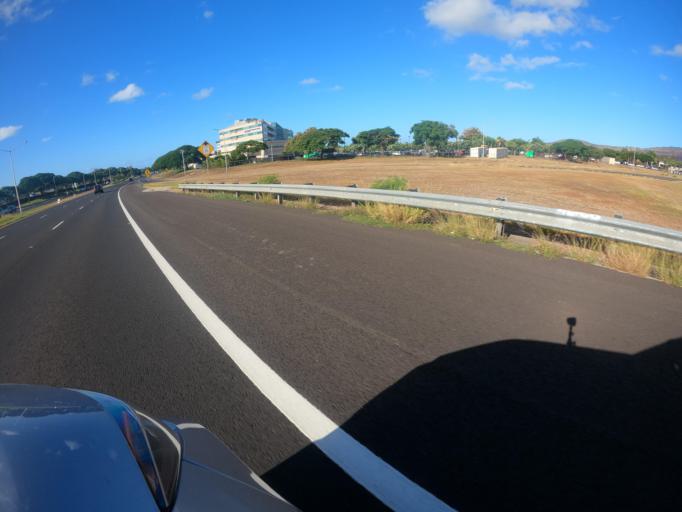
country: US
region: Hawaii
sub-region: Honolulu County
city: Royal Kunia
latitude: 21.3741
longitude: -158.0263
